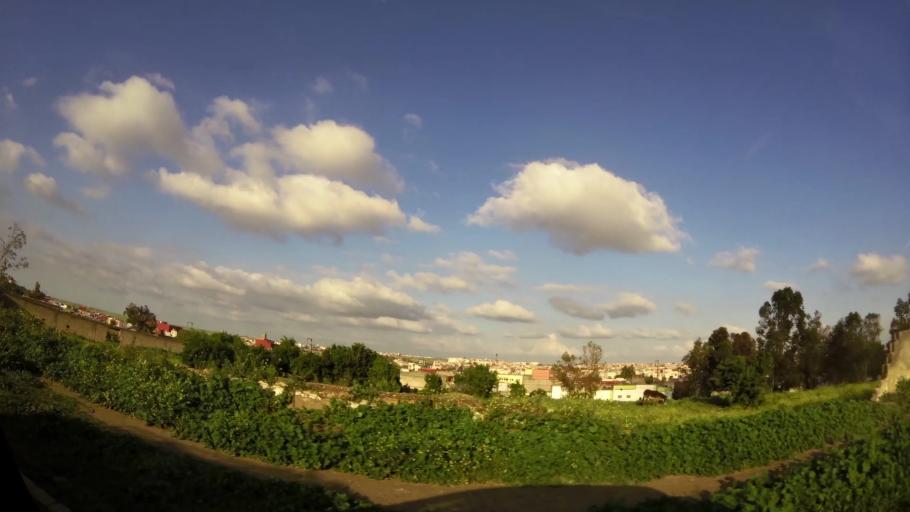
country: MA
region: Chaouia-Ouardigha
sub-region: Settat Province
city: Settat
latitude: 33.0003
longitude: -7.6268
